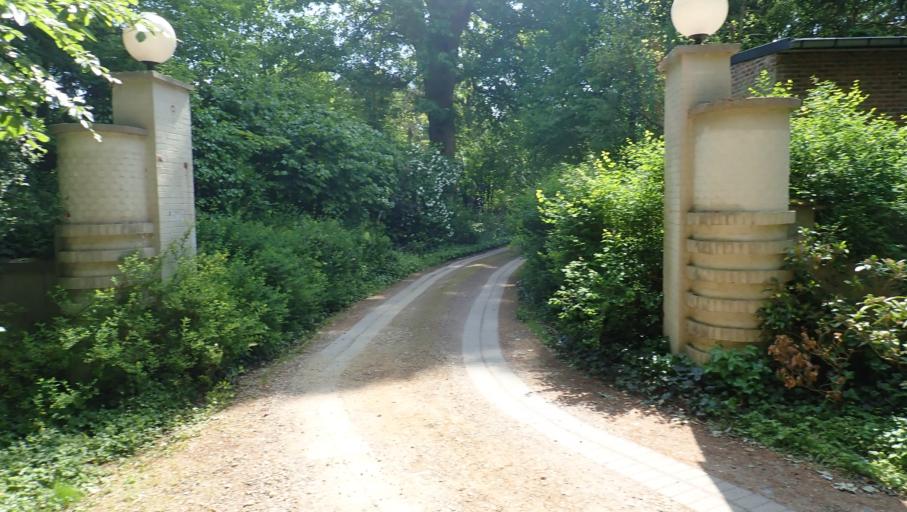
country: BE
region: Flanders
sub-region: Provincie Antwerpen
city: Zoersel
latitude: 51.2774
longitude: 4.6636
